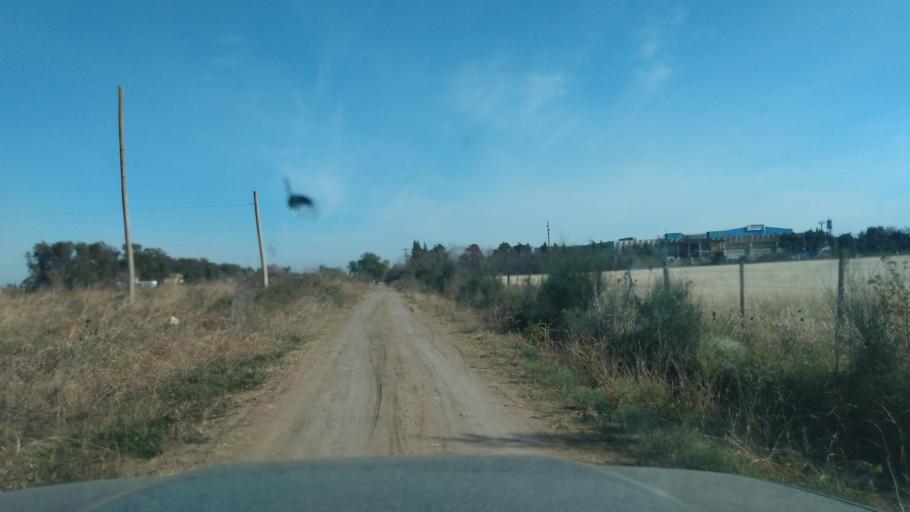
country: AR
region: Buenos Aires
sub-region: Partido de Lujan
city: Lujan
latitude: -34.5654
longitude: -59.1381
